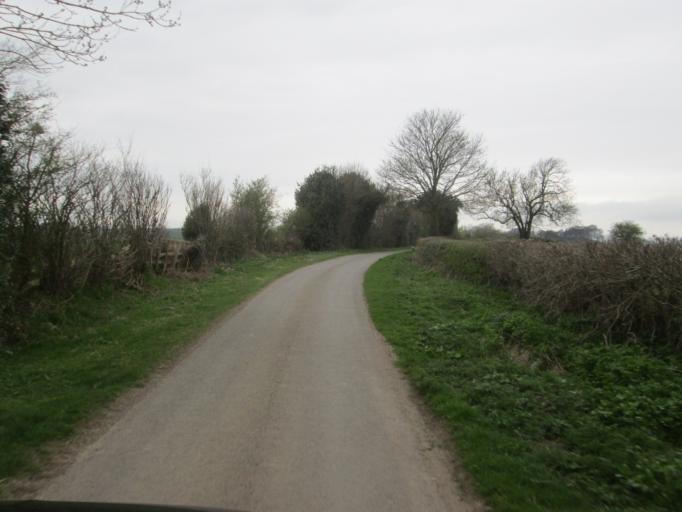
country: GB
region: England
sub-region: Derbyshire
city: Duffield
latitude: 52.9843
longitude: -1.5311
